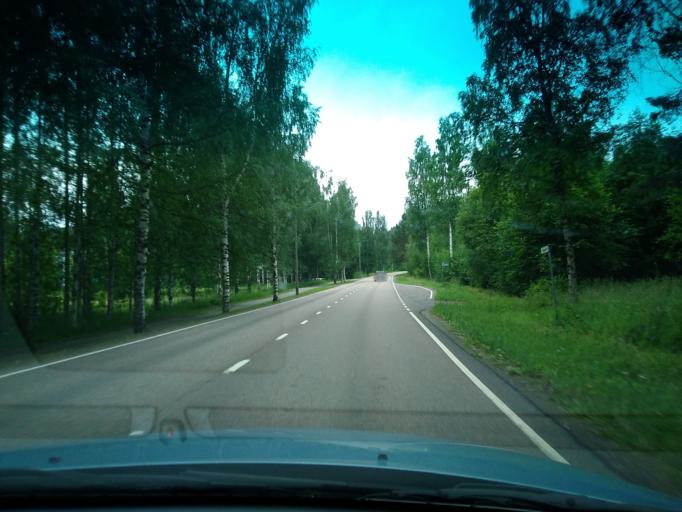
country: FI
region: Central Finland
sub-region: Keuruu
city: Multia
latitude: 62.4019
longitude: 24.7927
